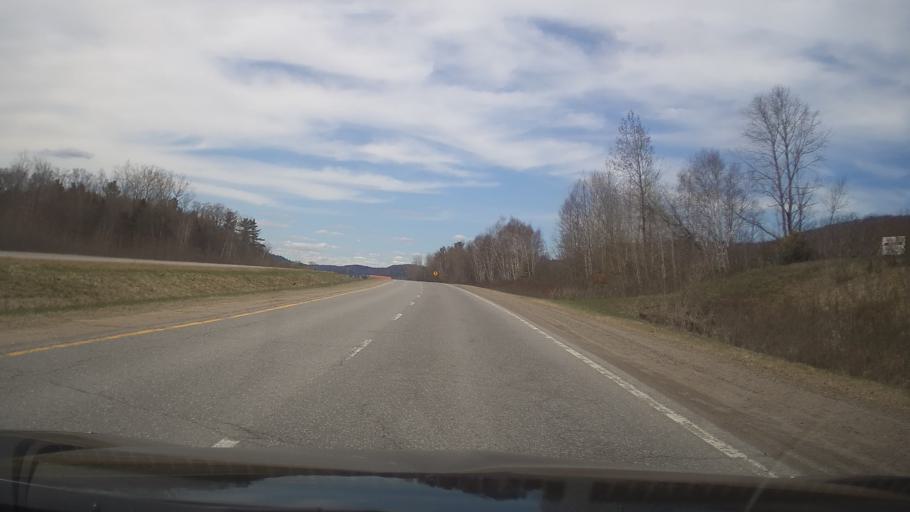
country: CA
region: Quebec
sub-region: Outaouais
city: Wakefield
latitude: 45.5320
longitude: -76.0071
